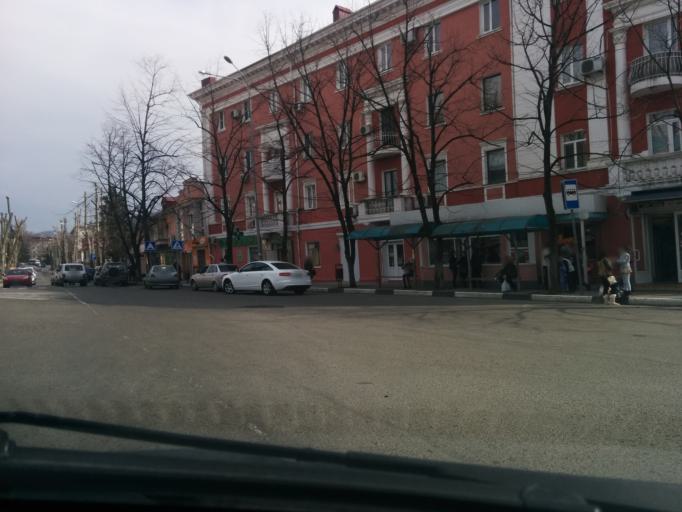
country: RU
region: Krasnodarskiy
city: Tuapse
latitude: 44.0994
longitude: 39.0795
